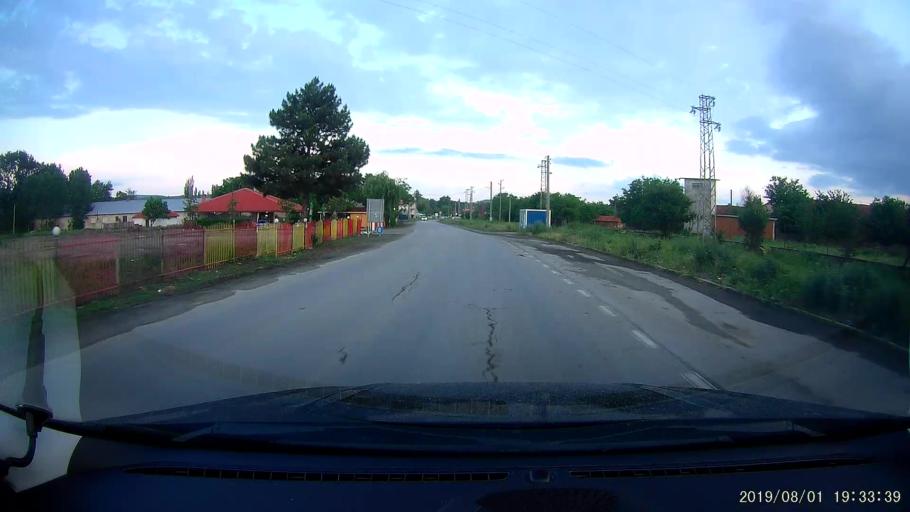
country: BG
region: Burgas
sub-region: Obshtina Sungurlare
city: Sungurlare
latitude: 42.7768
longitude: 26.8771
